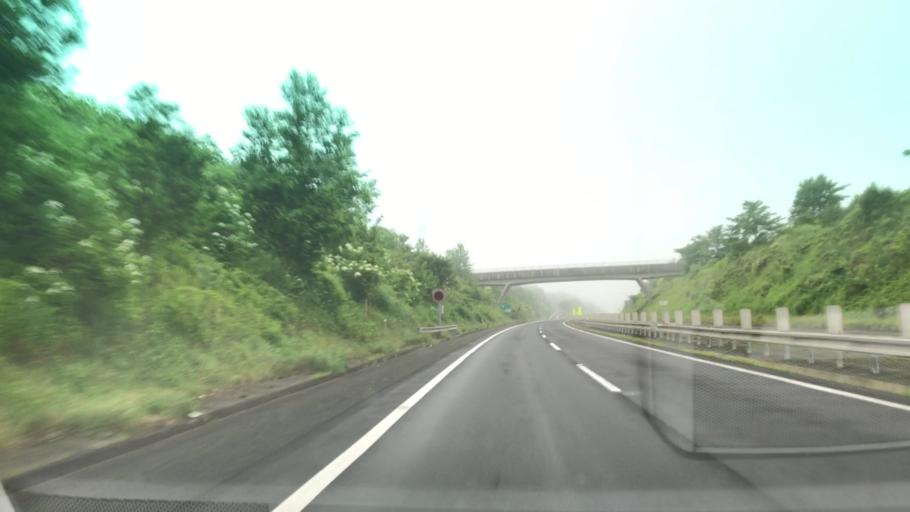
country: JP
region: Hokkaido
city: Muroran
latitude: 42.4471
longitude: 141.1551
